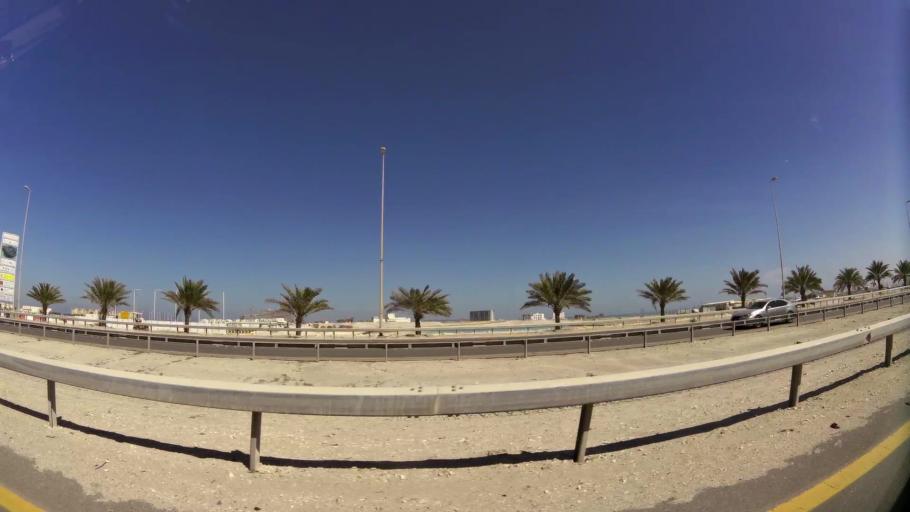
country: BH
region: Muharraq
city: Al Hadd
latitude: 26.2698
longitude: 50.6618
